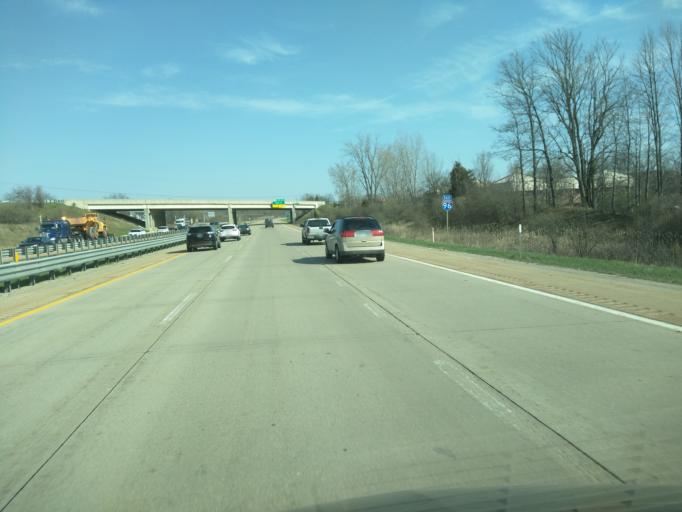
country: US
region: Michigan
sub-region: Kent County
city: Forest Hills
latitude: 42.9094
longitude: -85.5314
